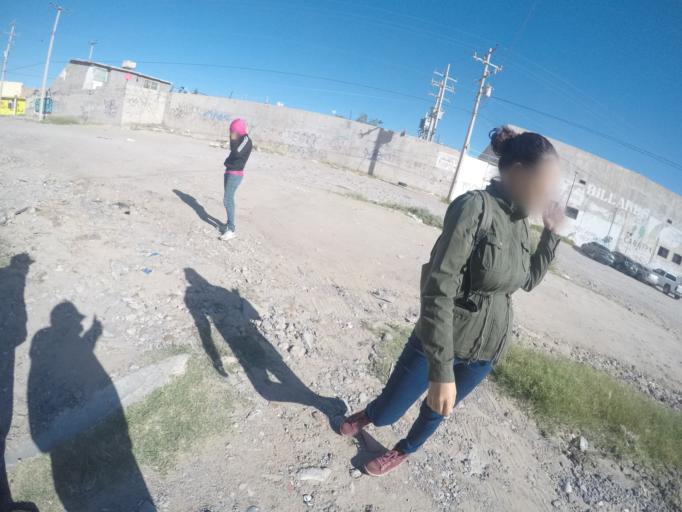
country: US
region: Texas
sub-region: El Paso County
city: Socorro
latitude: 31.6659
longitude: -106.4046
